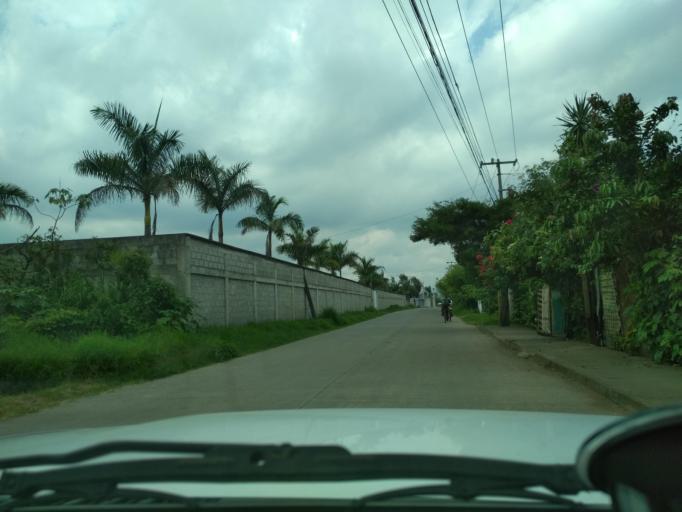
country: MX
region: Veracruz
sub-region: Ixtaczoquitlan
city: Buenavista
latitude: 18.8853
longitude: -97.0483
